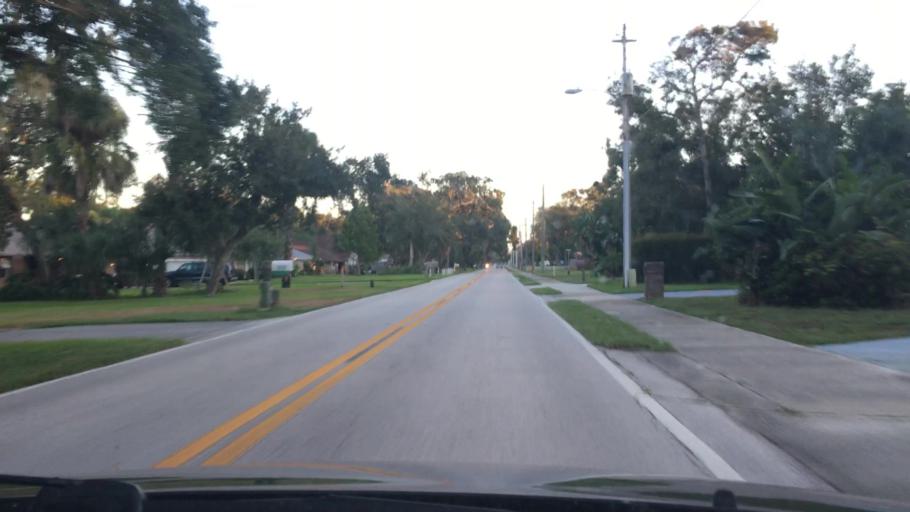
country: US
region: Florida
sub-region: Volusia County
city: Ormond-by-the-Sea
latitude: 29.3191
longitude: -81.0725
